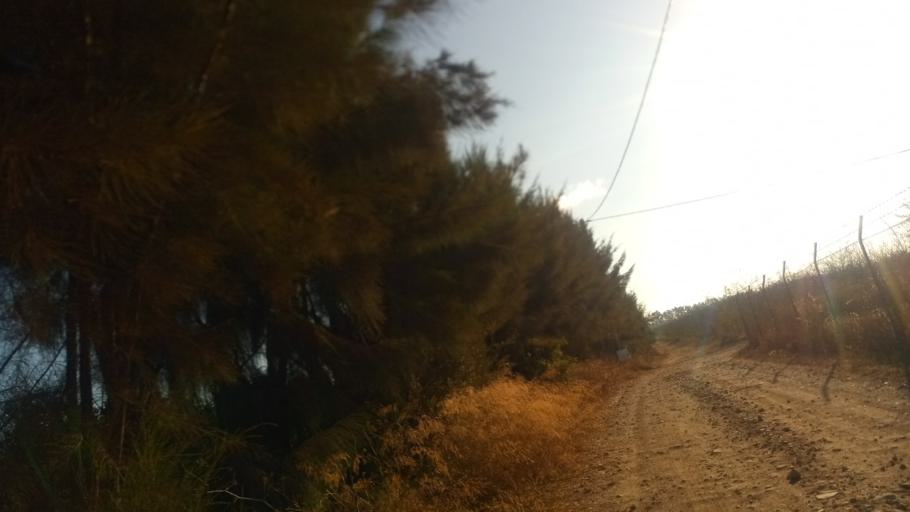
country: PT
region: Faro
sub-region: Tavira
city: Tavira
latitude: 37.1469
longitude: -7.5846
